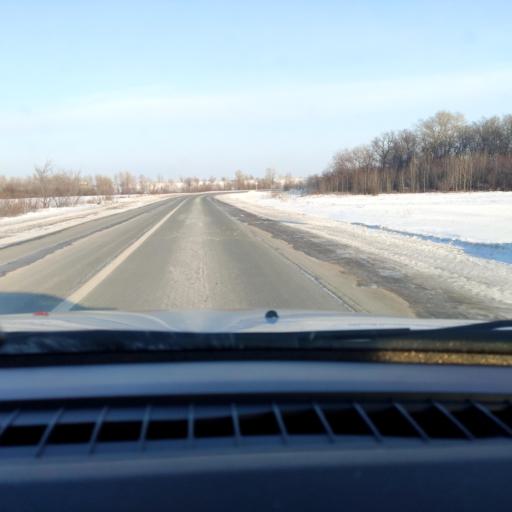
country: RU
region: Samara
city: Kinel'
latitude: 53.1866
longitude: 50.5075
